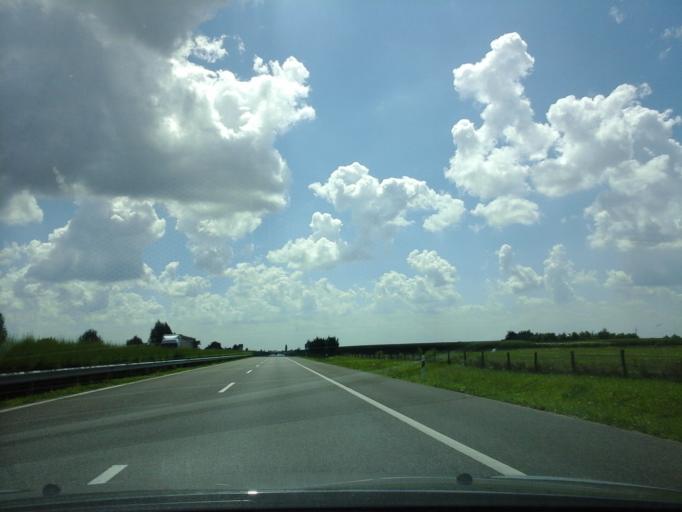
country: HU
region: Hajdu-Bihar
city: Ebes
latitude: 47.5157
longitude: 21.5493
